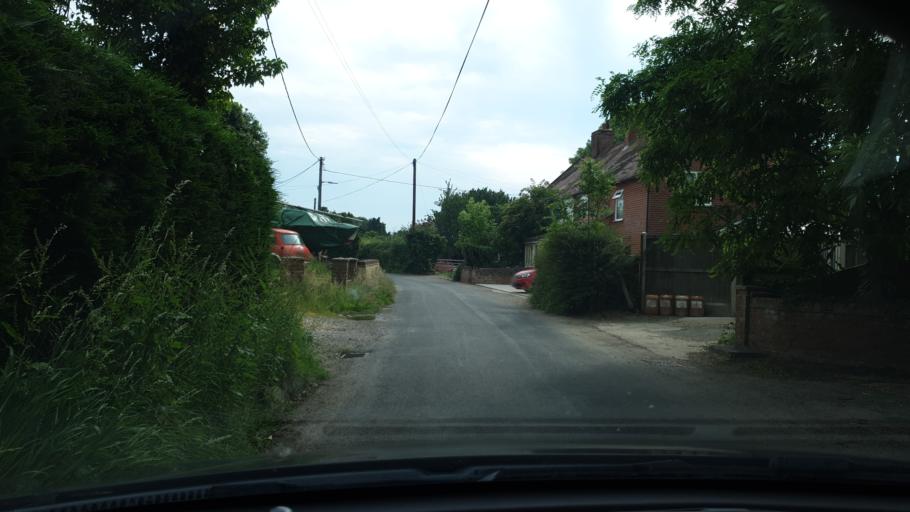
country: GB
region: England
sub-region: Essex
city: Dovercourt
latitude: 51.9165
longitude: 1.2122
